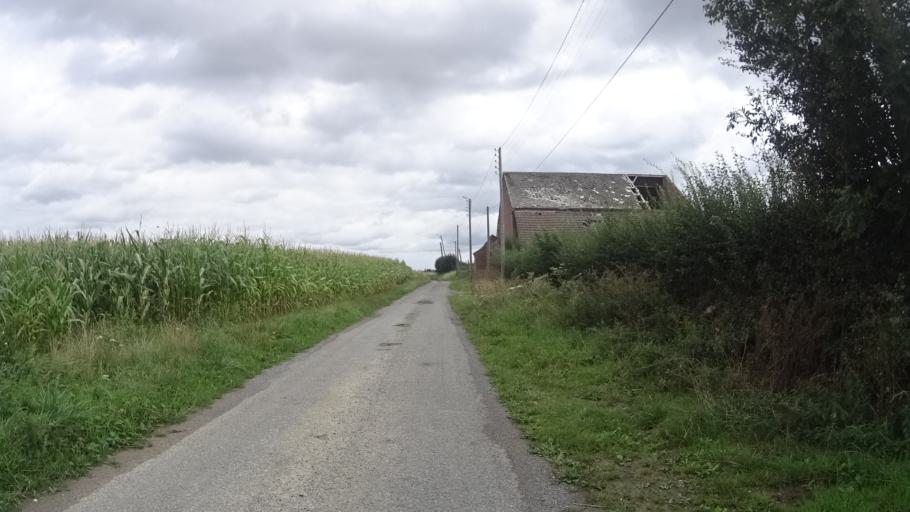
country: FR
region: Nord-Pas-de-Calais
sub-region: Departement du Nord
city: Pont-sur-Sambre
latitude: 50.2130
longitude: 3.8420
